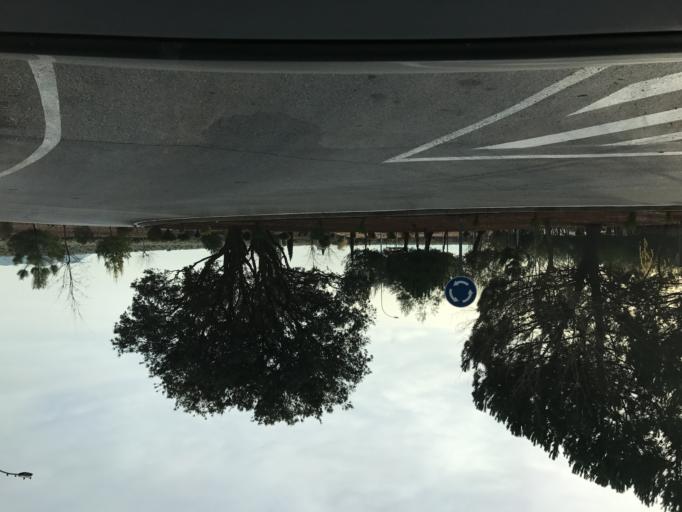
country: ES
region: Andalusia
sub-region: Provincia de Granada
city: Colomera
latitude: 37.3298
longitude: -3.6765
